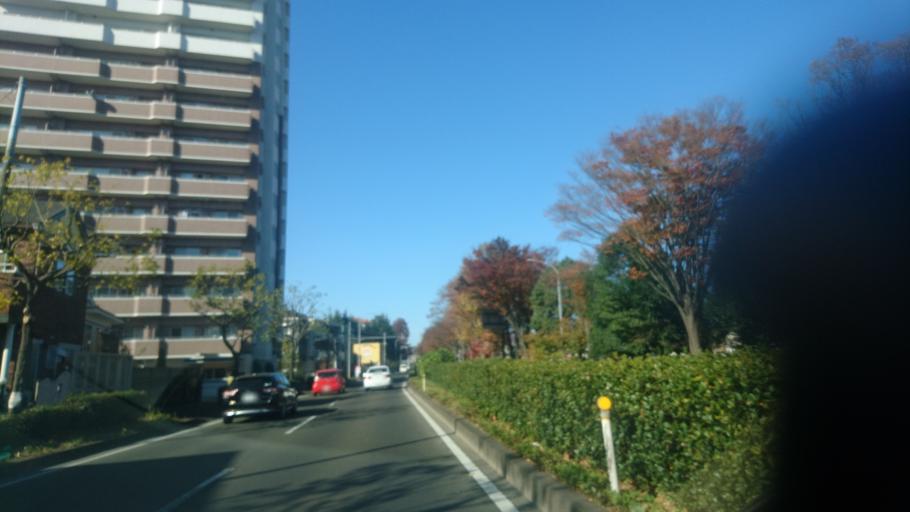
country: JP
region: Miyagi
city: Sendai
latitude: 38.2360
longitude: 140.8875
